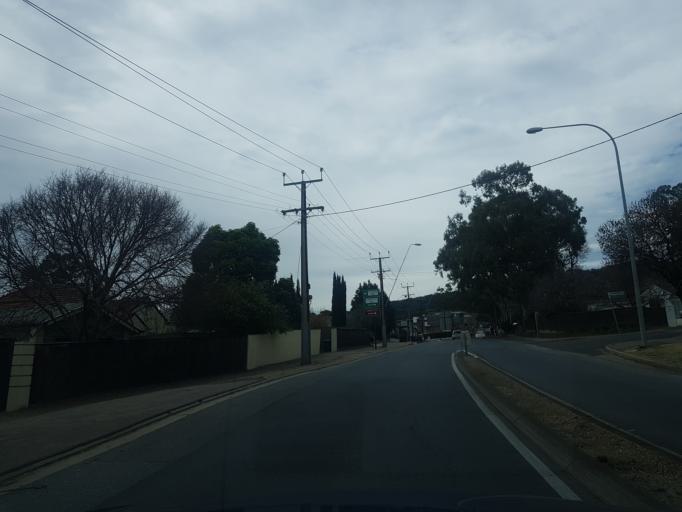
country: AU
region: South Australia
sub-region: Mitcham
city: Mitcham
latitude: -34.9777
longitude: 138.6255
